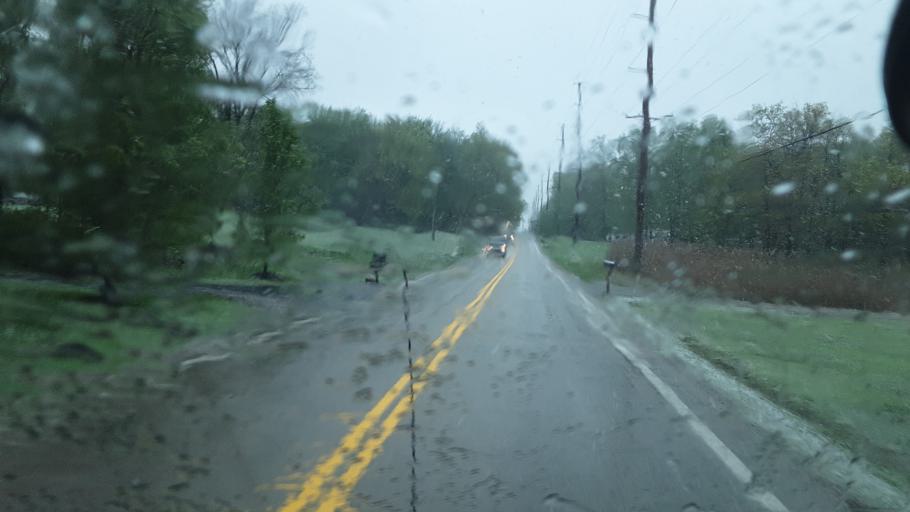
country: US
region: Ohio
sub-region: Portage County
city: Windham
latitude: 41.3092
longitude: -80.9946
